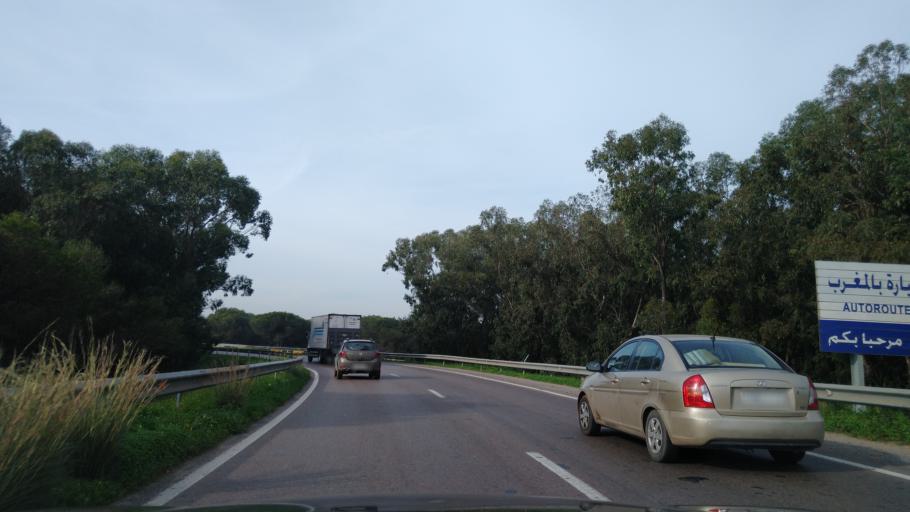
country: MA
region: Rabat-Sale-Zemmour-Zaer
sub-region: Skhirate-Temara
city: Temara
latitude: 33.9502
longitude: -6.9188
